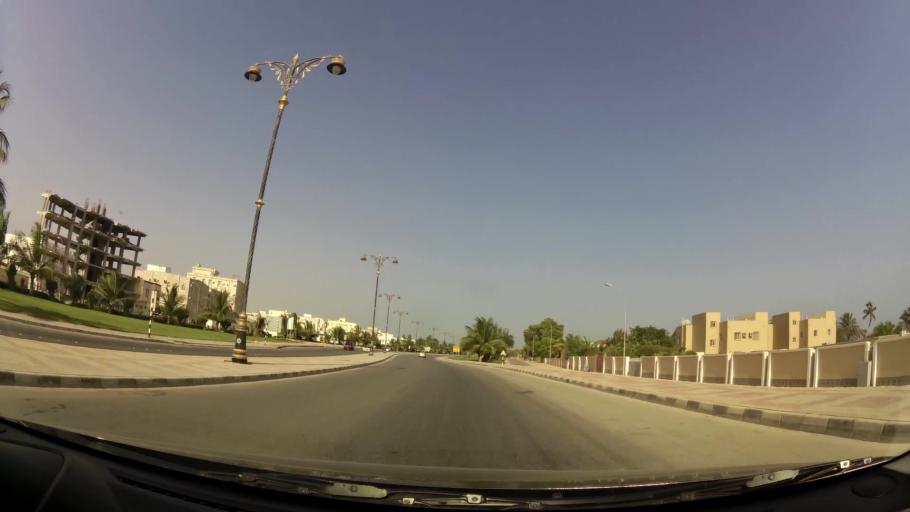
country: OM
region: Zufar
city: Salalah
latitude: 17.0039
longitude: 54.0598
